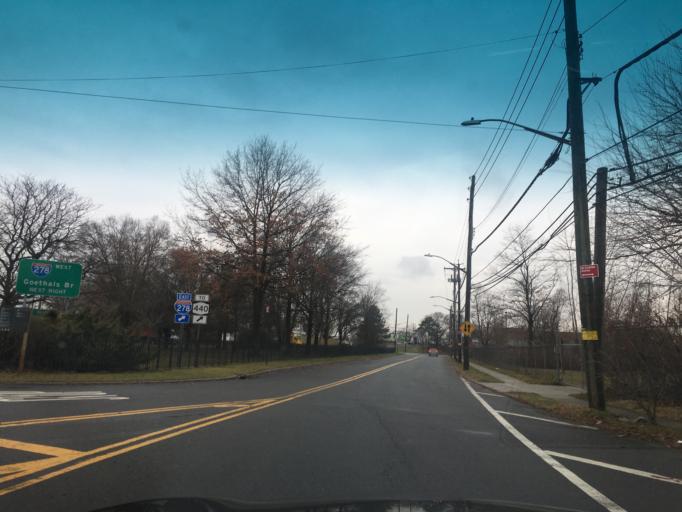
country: US
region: New York
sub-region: Richmond County
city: Bloomfield
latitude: 40.6261
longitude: -74.1760
